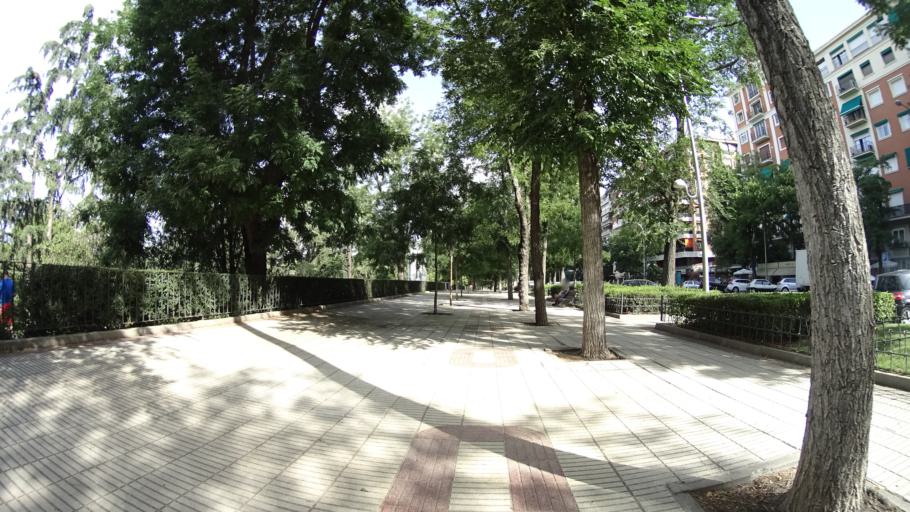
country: ES
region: Madrid
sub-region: Provincia de Madrid
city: Moncloa-Aravaca
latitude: 40.4263
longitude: -3.7195
